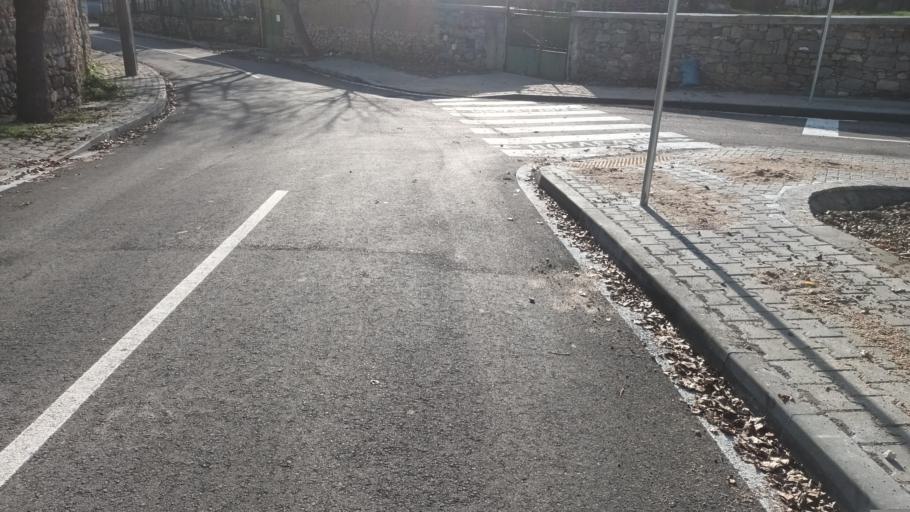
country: BG
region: Plovdiv
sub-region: Obshtina Khisarya
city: Khisarya
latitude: 42.5214
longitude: 24.7211
